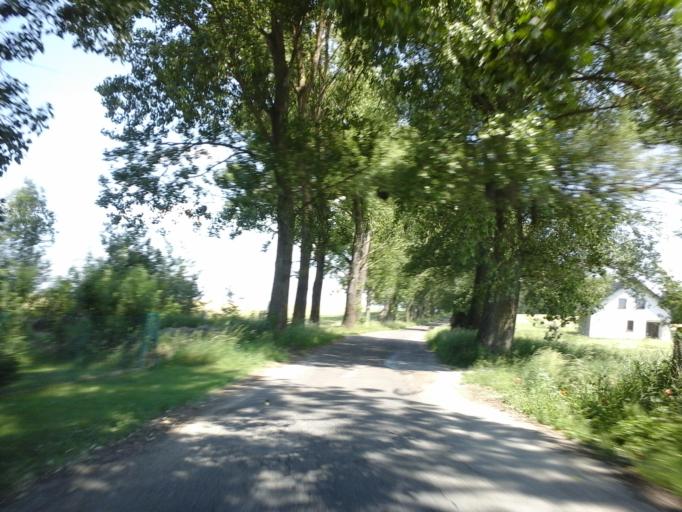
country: PL
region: West Pomeranian Voivodeship
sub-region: Powiat choszczenski
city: Choszczno
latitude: 53.1480
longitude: 15.3532
